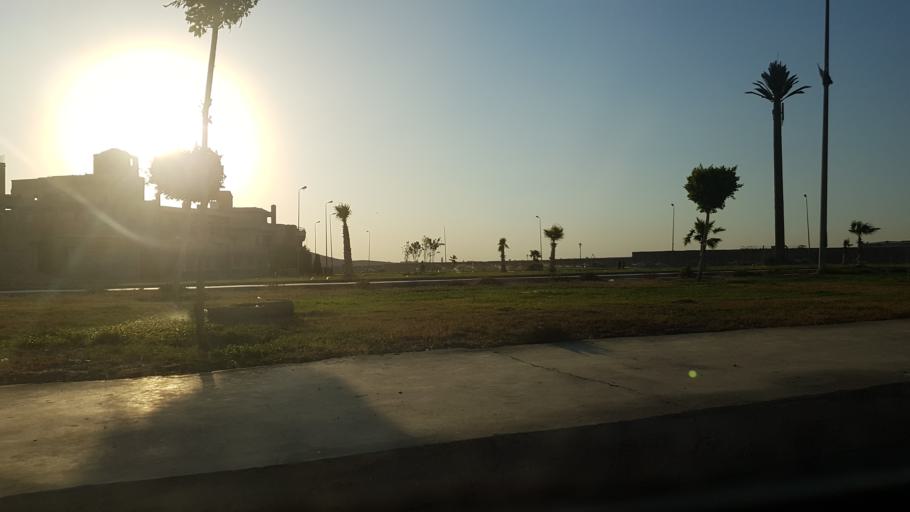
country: EG
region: Muhafazat al Qalyubiyah
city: Al Khankah
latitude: 30.0457
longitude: 31.4423
